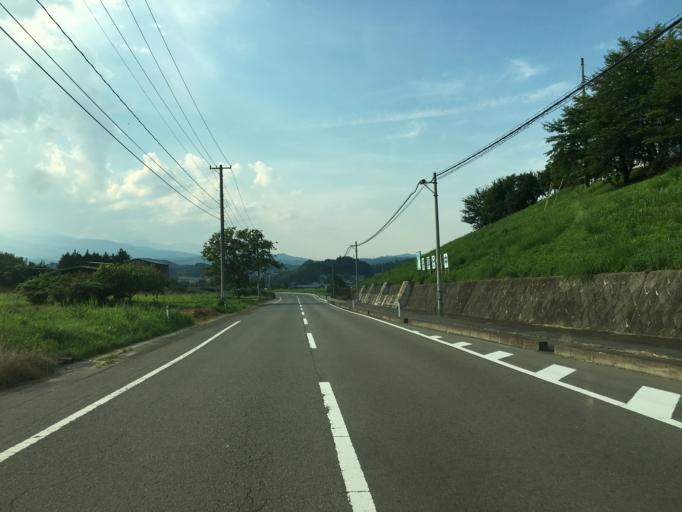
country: JP
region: Fukushima
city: Nihommatsu
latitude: 37.5572
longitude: 140.4308
